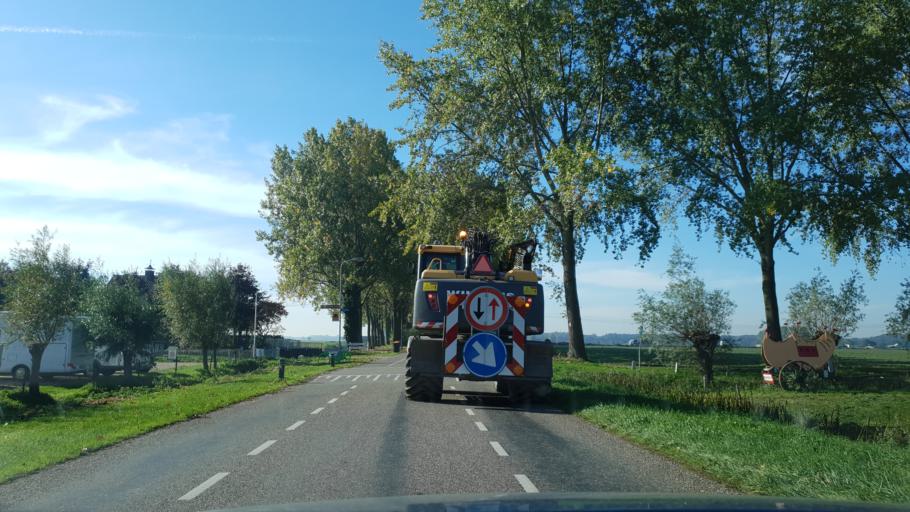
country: NL
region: Gelderland
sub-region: Gemeente Wijchen
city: Bergharen
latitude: 51.8689
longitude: 5.6950
